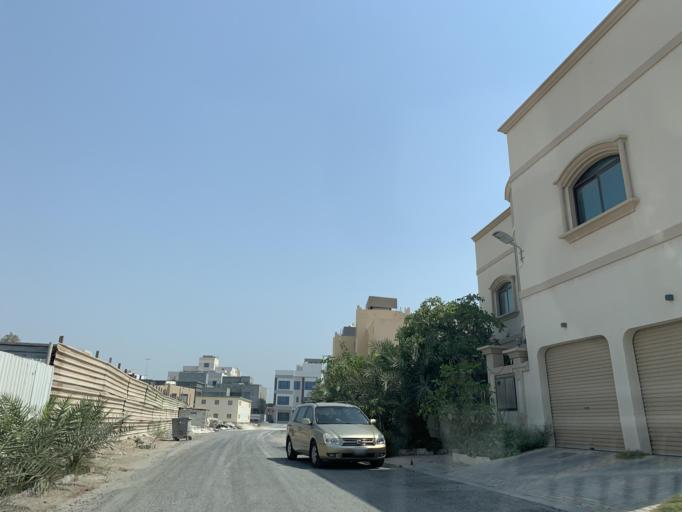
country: BH
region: Manama
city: Jidd Hafs
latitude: 26.2155
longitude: 50.5229
